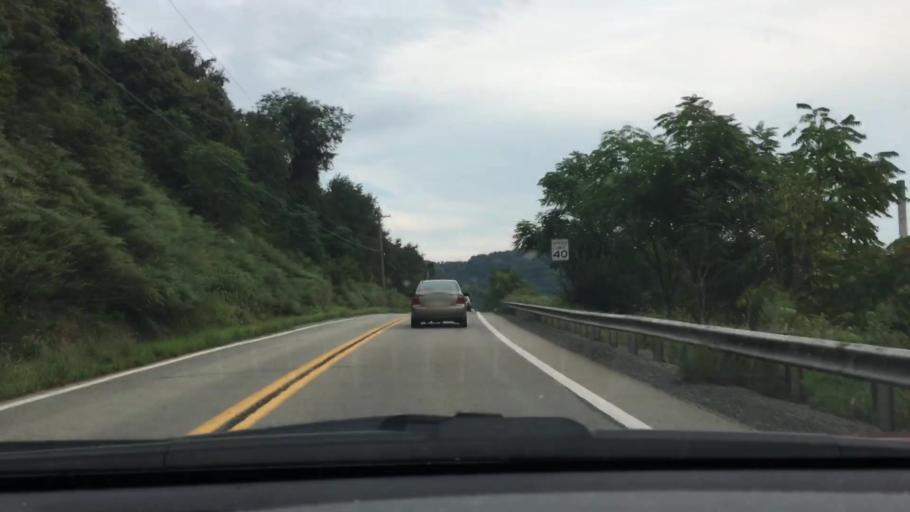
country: US
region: Pennsylvania
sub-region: Allegheny County
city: Wilson
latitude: 40.3109
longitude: -79.8758
